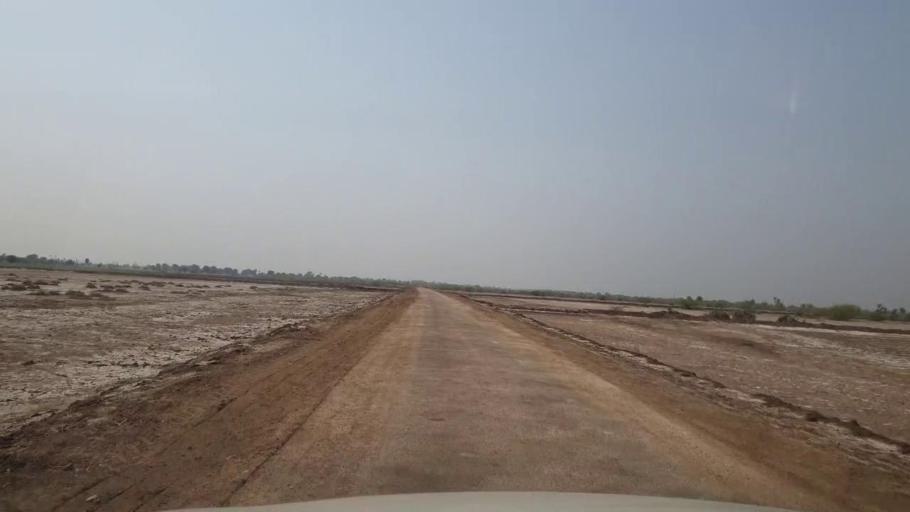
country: PK
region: Sindh
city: Umarkot
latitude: 25.4491
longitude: 69.6935
